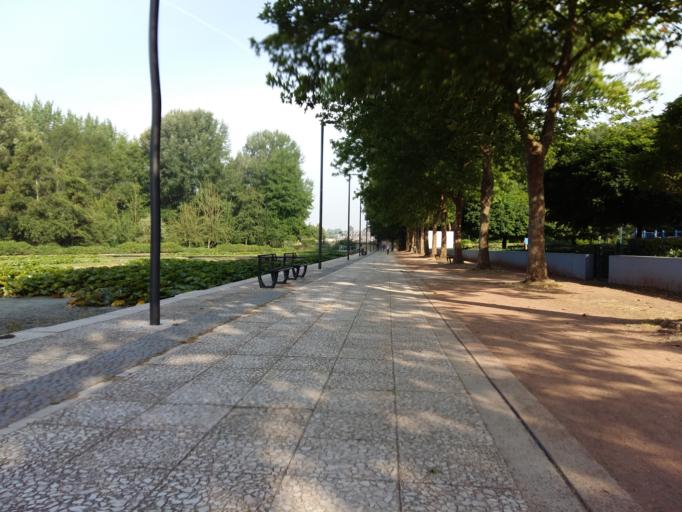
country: FR
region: Picardie
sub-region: Departement de la Somme
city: Amiens
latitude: 49.9005
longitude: 2.3073
